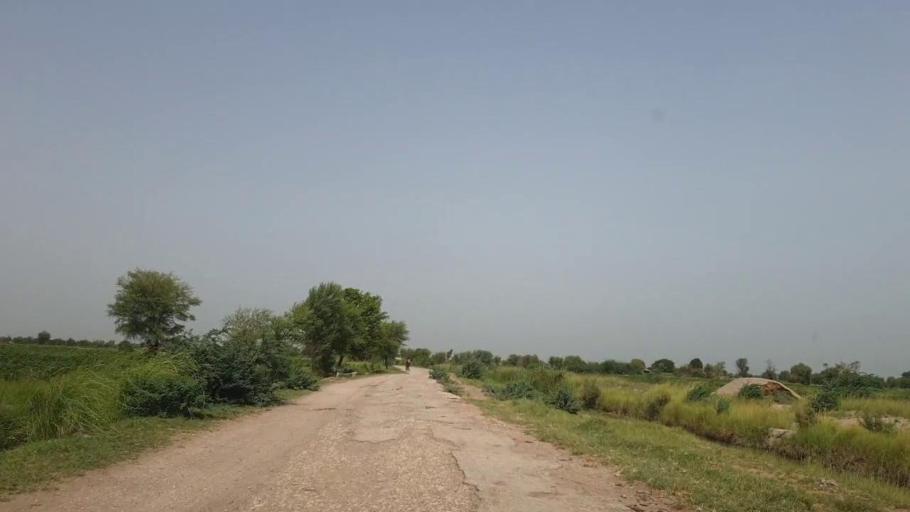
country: PK
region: Sindh
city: Sakrand
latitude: 26.1286
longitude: 68.3673
